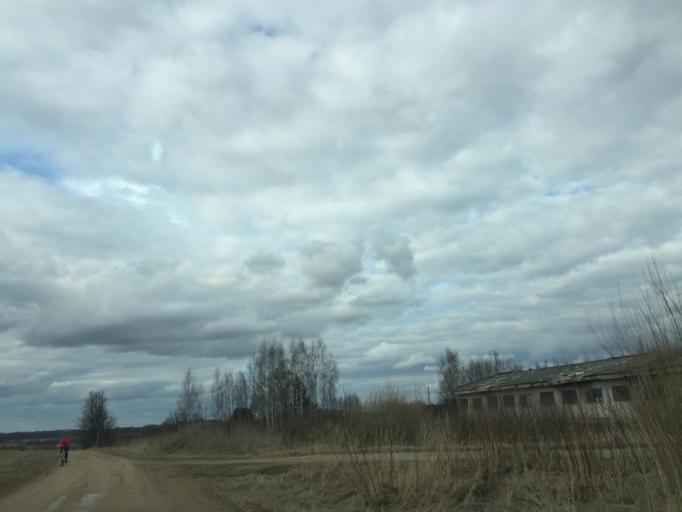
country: LV
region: Lielvarde
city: Lielvarde
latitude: 56.5107
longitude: 24.7384
